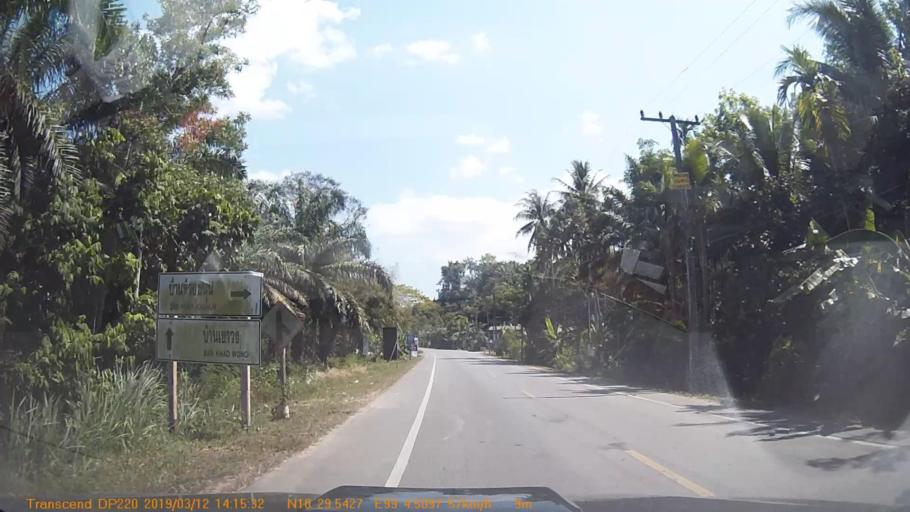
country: TH
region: Chumphon
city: Chumphon
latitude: 10.4921
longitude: 99.0752
